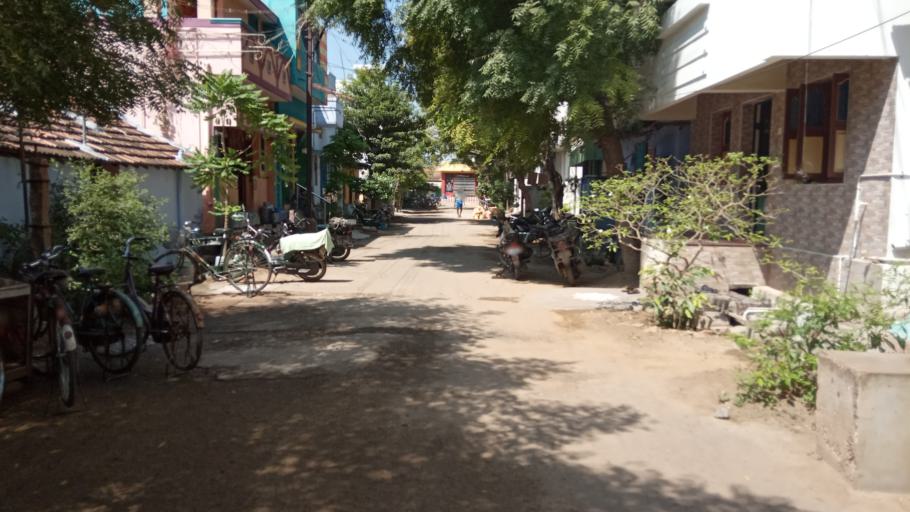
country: IN
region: Tamil Nadu
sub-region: Virudhunagar
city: Aruppukkottai
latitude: 9.5099
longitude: 78.0878
